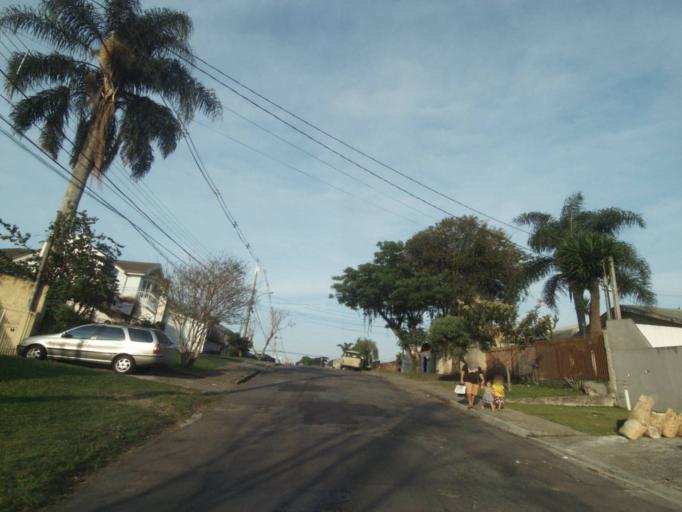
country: BR
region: Parana
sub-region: Curitiba
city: Curitiba
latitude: -25.4636
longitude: -49.3111
